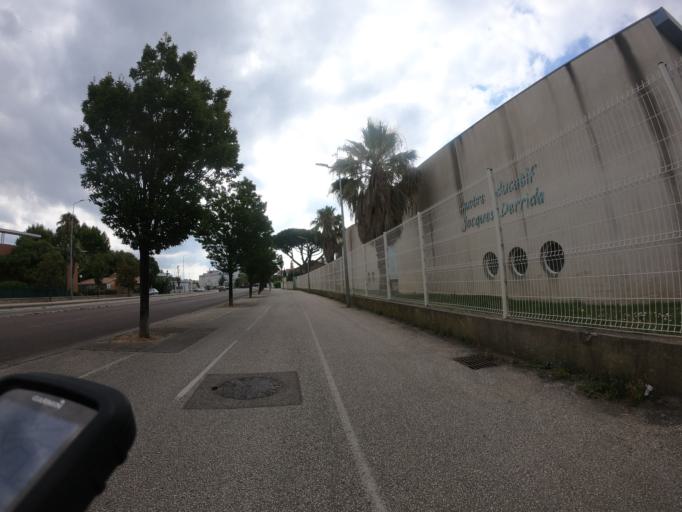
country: FR
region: Provence-Alpes-Cote d'Azur
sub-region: Departement du Var
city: La Seyne-sur-Mer
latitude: 43.1067
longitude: 5.8711
